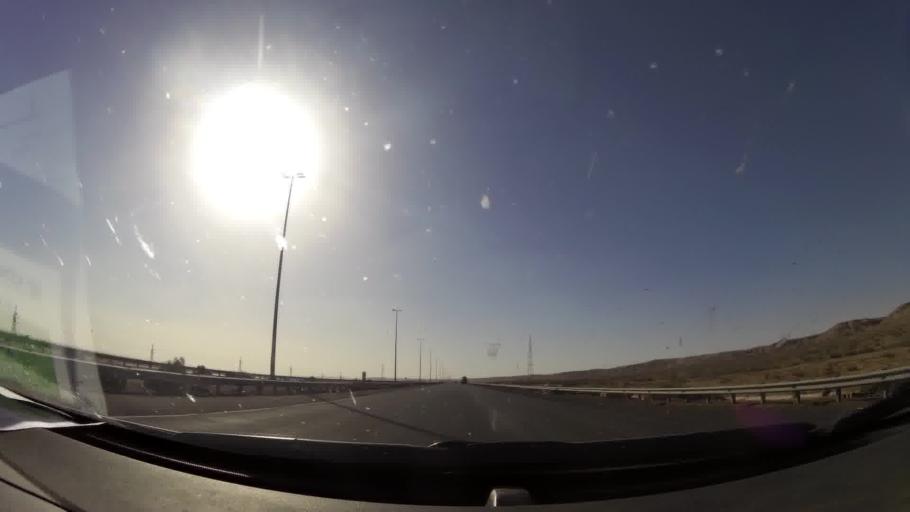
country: KW
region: Al Asimah
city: Kuwait City
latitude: 29.5375
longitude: 47.8433
